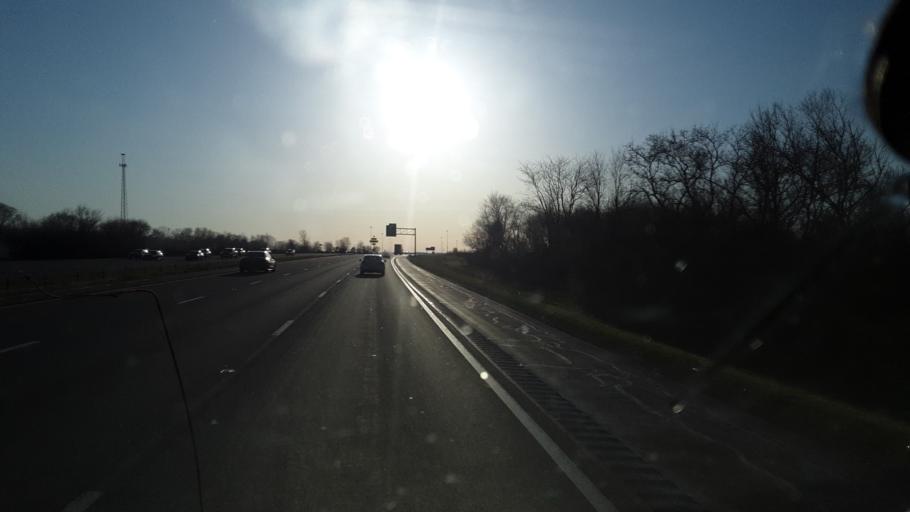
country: US
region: Ohio
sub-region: Medina County
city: Lodi
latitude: 40.9988
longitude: -81.9794
